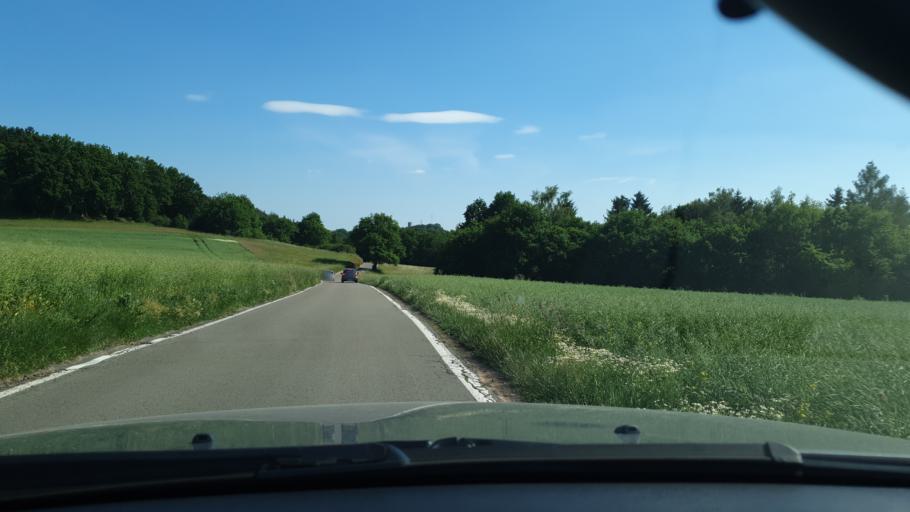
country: DE
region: Rheinland-Pfalz
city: Otterberg
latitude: 49.4867
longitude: 7.7694
